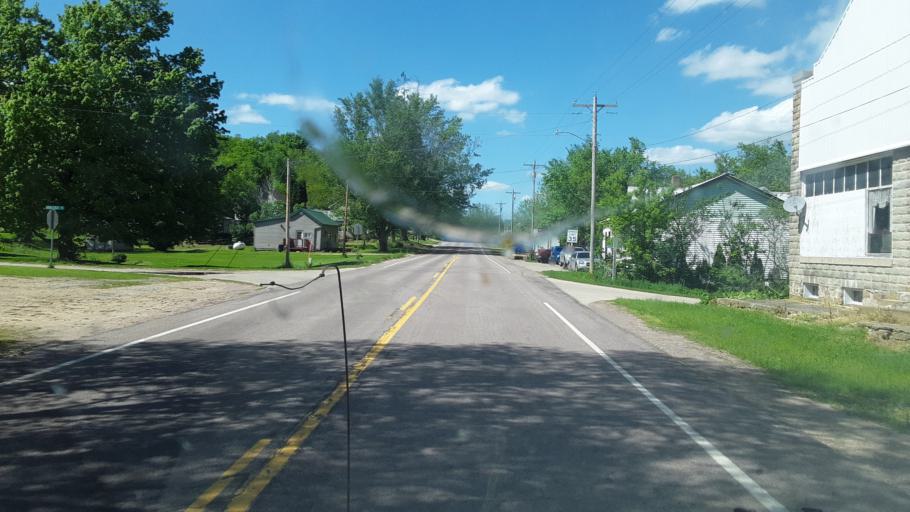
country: US
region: Wisconsin
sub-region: Richland County
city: Richland Center
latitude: 43.4219
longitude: -90.2434
